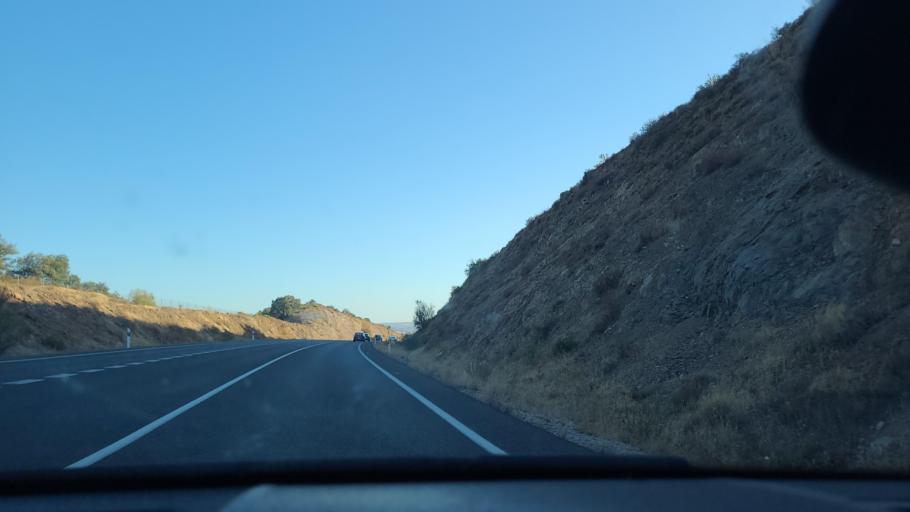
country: ES
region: Andalusia
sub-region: Province of Cordoba
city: Cordoba
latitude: 37.9398
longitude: -4.7624
